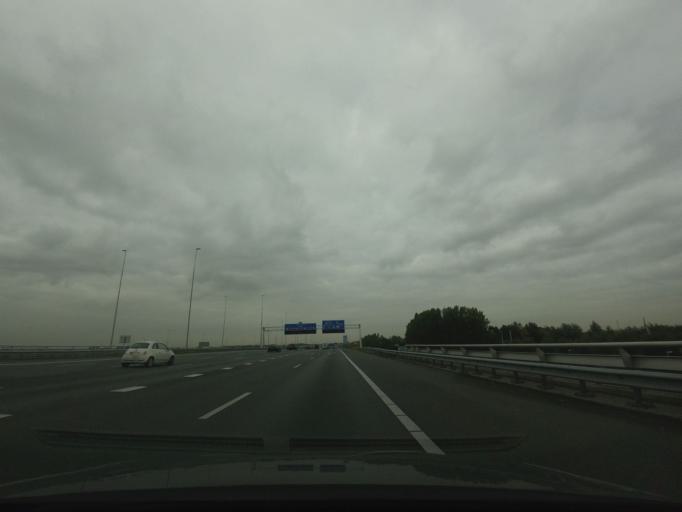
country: NL
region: North Holland
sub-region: Gemeente Amsterdam
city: Amsterdam-Zuidoost
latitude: 52.2784
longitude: 4.9547
